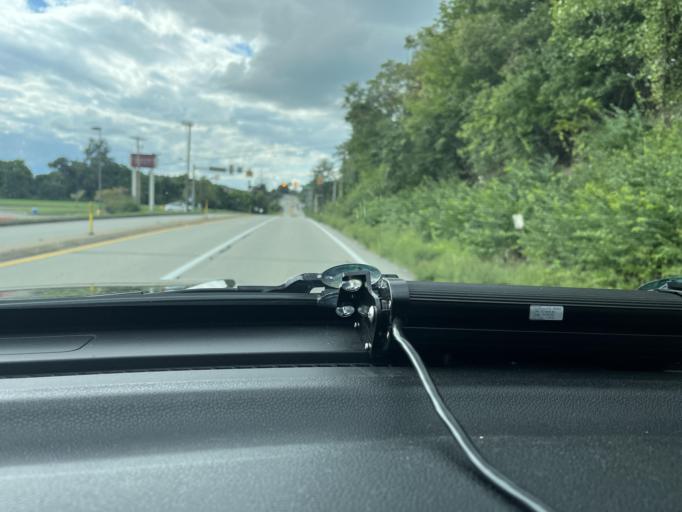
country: US
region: Pennsylvania
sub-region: Fayette County
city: South Uniontown
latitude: 39.9104
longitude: -79.7507
